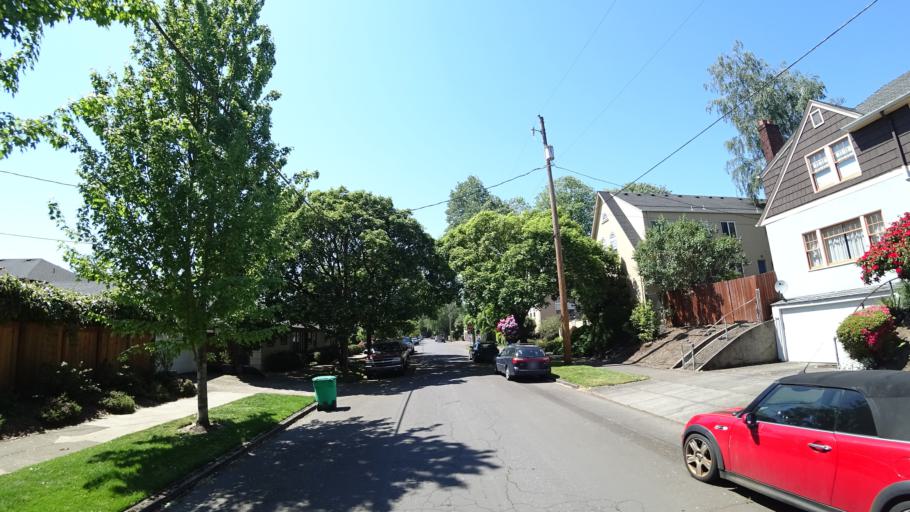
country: US
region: Oregon
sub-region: Multnomah County
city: Portland
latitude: 45.5406
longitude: -122.6559
